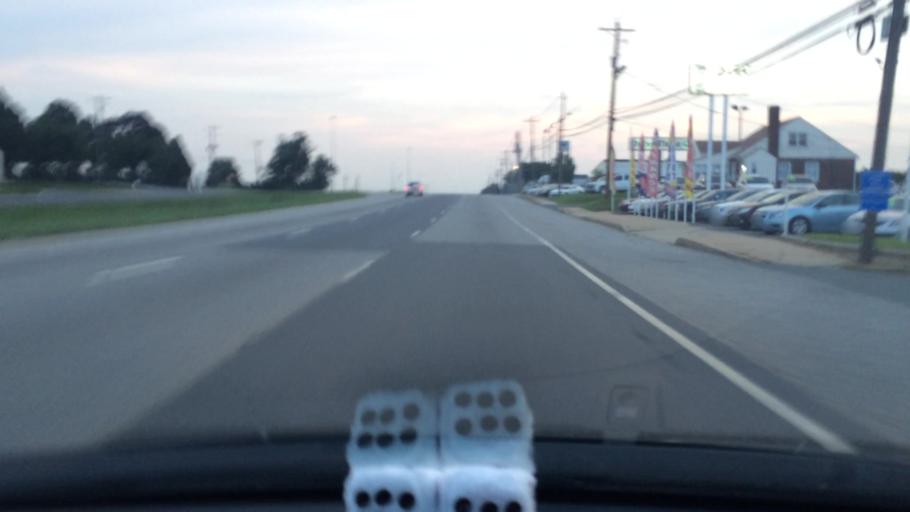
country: US
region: Delaware
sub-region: New Castle County
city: Wilmington Manor
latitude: 39.7045
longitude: -75.5691
